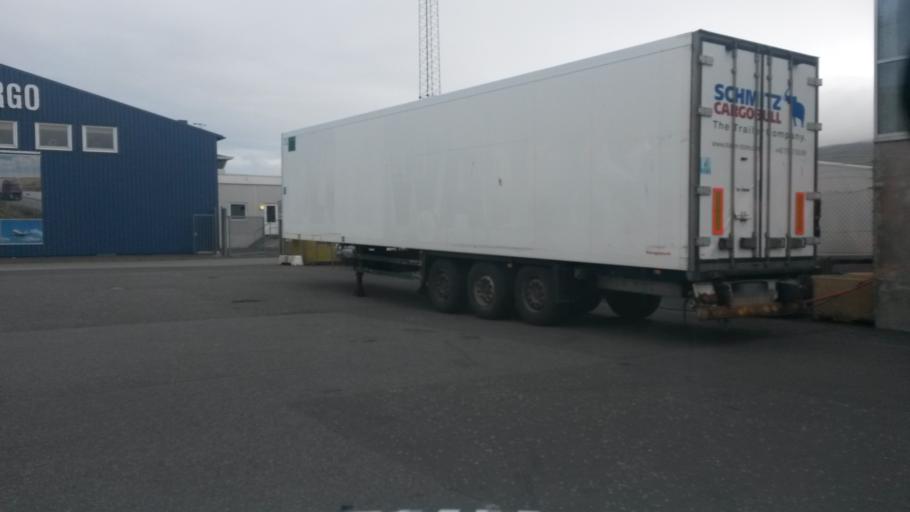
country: FO
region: Streymoy
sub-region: Torshavn
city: Torshavn
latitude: 62.0078
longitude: -6.7650
